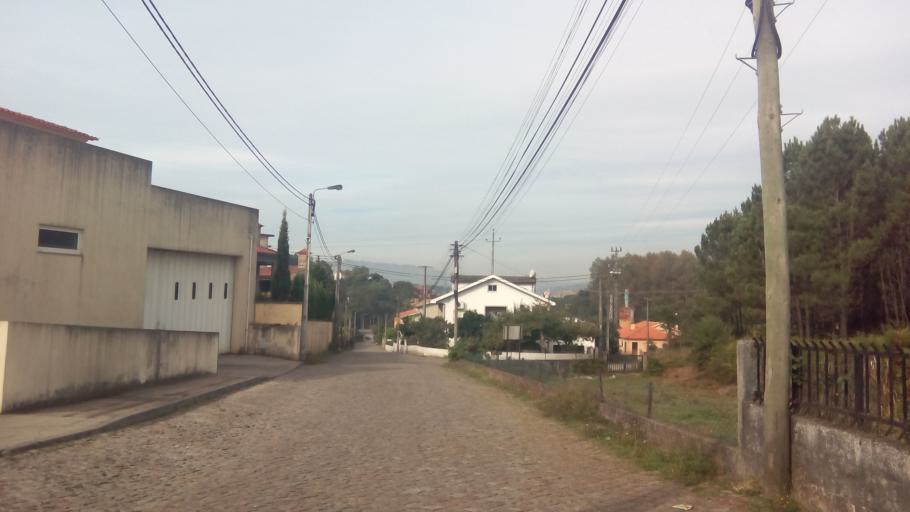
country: PT
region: Porto
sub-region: Paredes
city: Gandra
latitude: 41.1856
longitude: -8.4324
